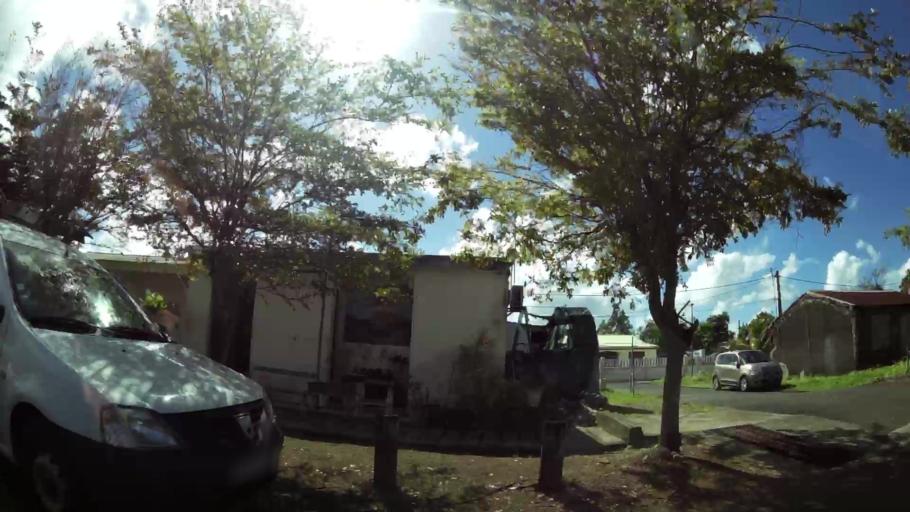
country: GP
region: Guadeloupe
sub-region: Guadeloupe
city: Port-Louis
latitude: 16.4207
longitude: -61.5305
